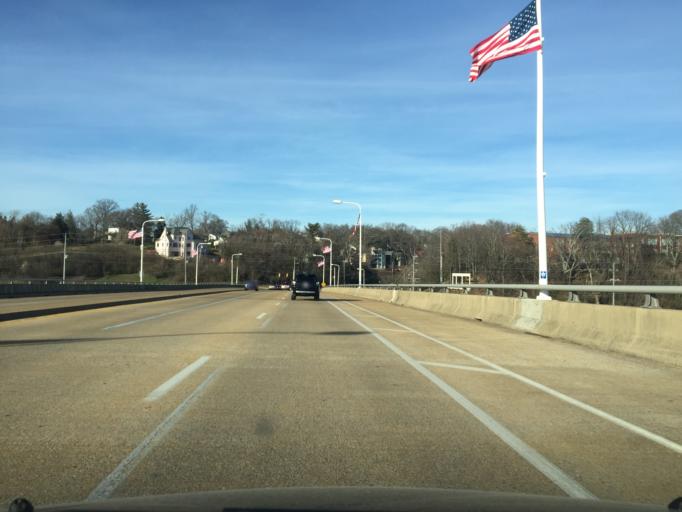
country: US
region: Tennessee
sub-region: Hamilton County
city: Chattanooga
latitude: 35.0590
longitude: -85.3021
